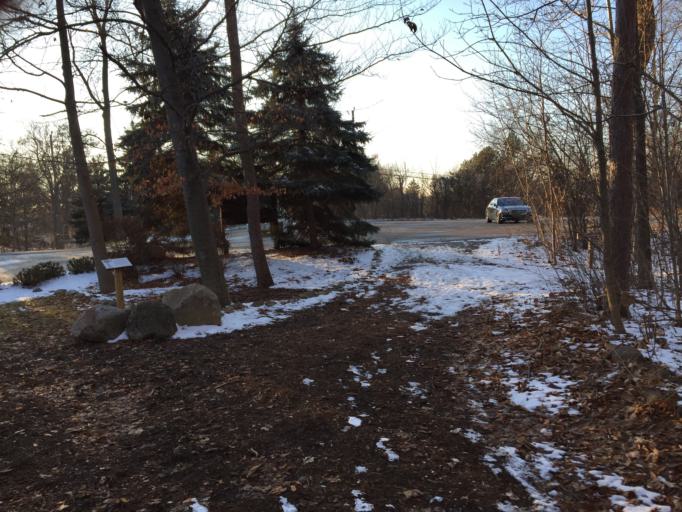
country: US
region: Michigan
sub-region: Oakland County
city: Bloomfield Hills
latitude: 42.5917
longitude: -83.2859
